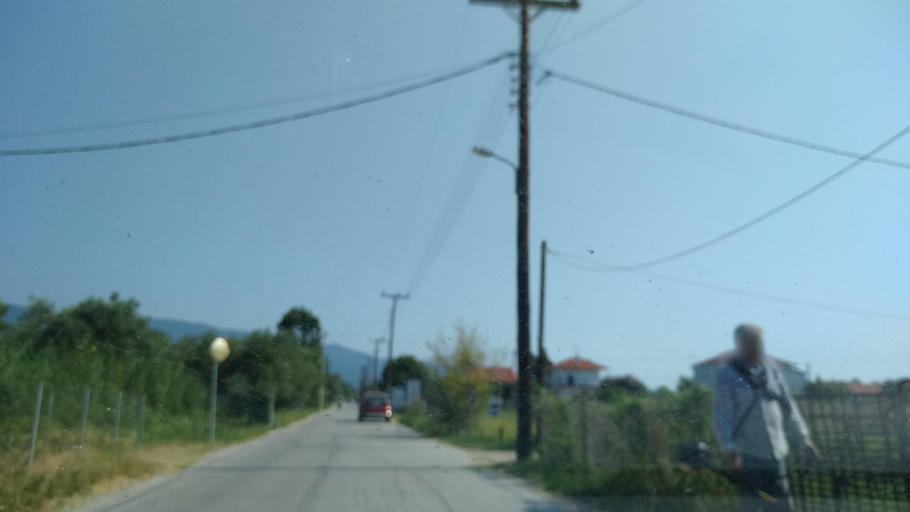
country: GR
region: Central Macedonia
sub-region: Nomos Thessalonikis
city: Nea Vrasna
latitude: 40.6869
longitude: 23.6887
